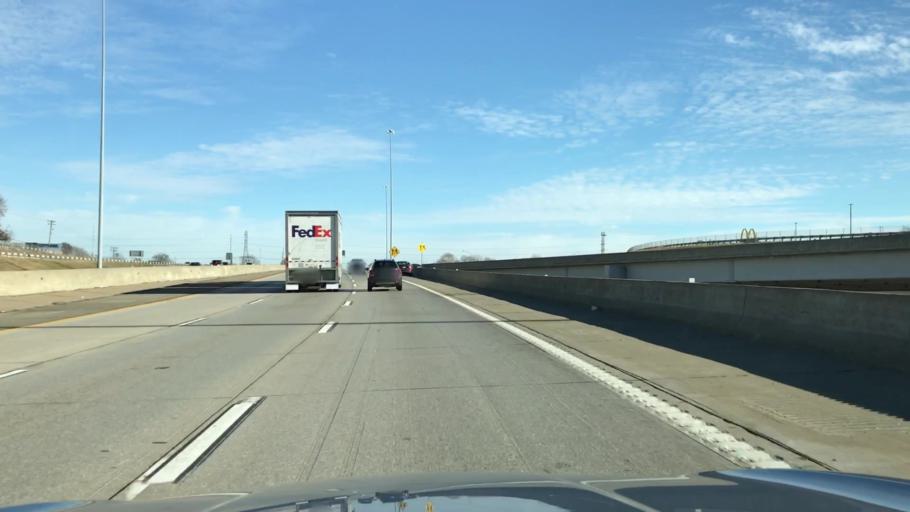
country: US
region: Missouri
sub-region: Saint Louis County
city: Florissant
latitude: 38.7755
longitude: -90.3392
